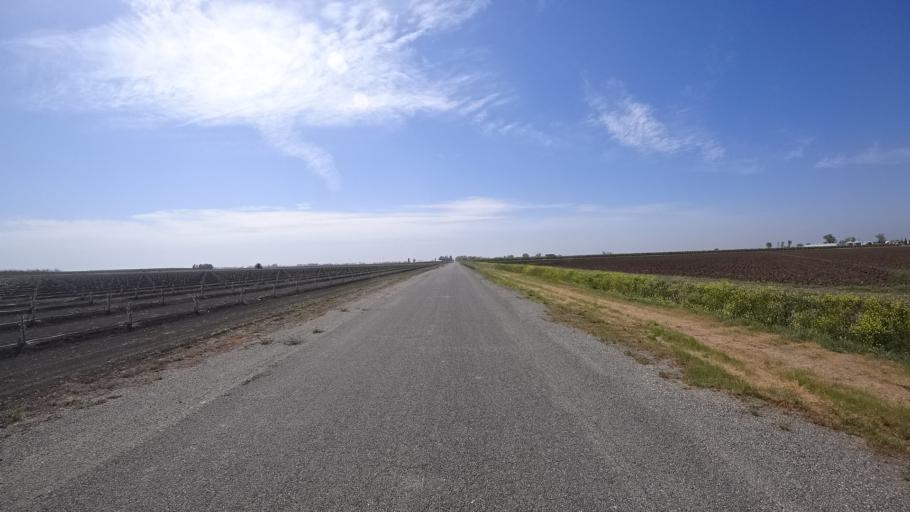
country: US
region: California
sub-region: Glenn County
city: Hamilton City
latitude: 39.6190
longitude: -122.0556
